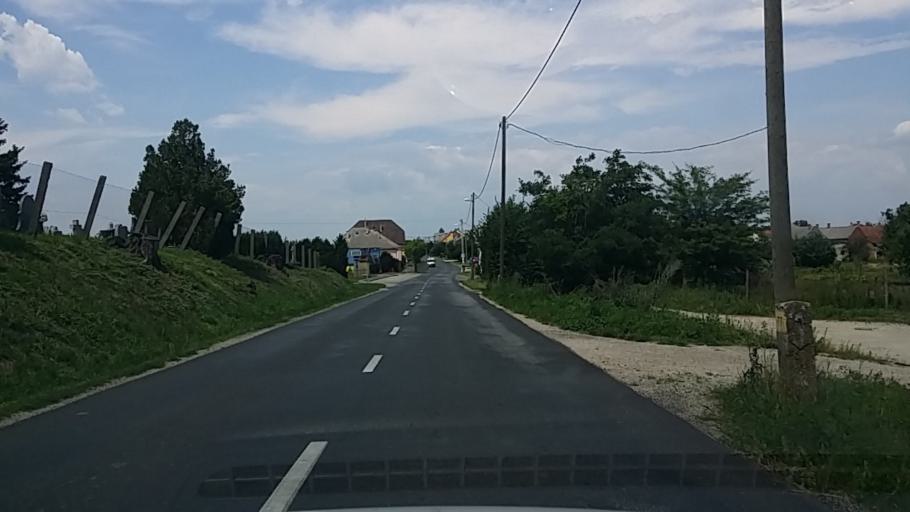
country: HU
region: Zala
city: Nagykanizsa
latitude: 46.4470
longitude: 16.9555
